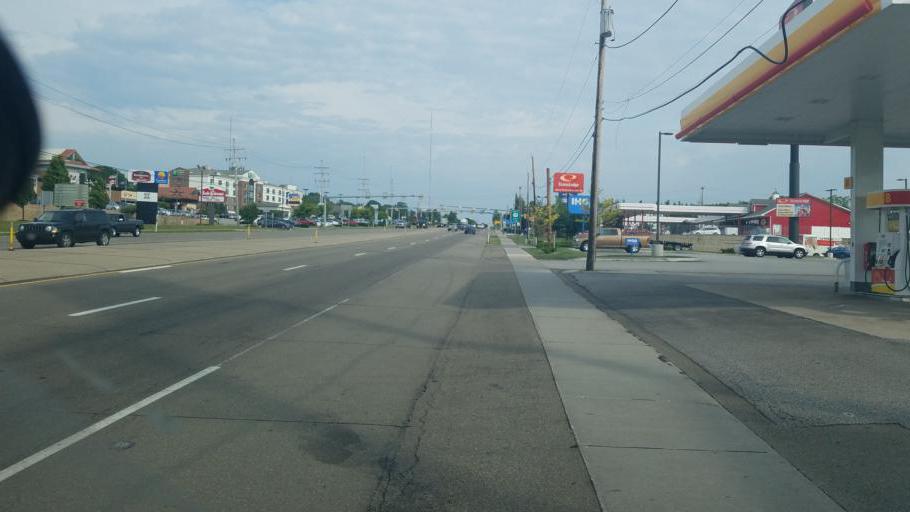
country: US
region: Pennsylvania
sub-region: Erie County
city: Erie
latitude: 42.0488
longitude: -80.0809
